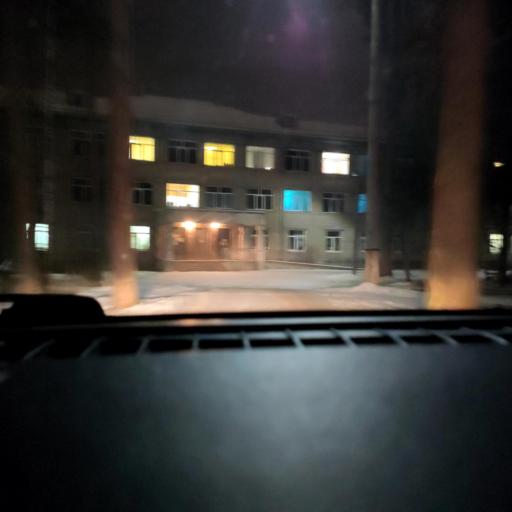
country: RU
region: Perm
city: Kondratovo
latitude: 57.9752
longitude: 56.1460
